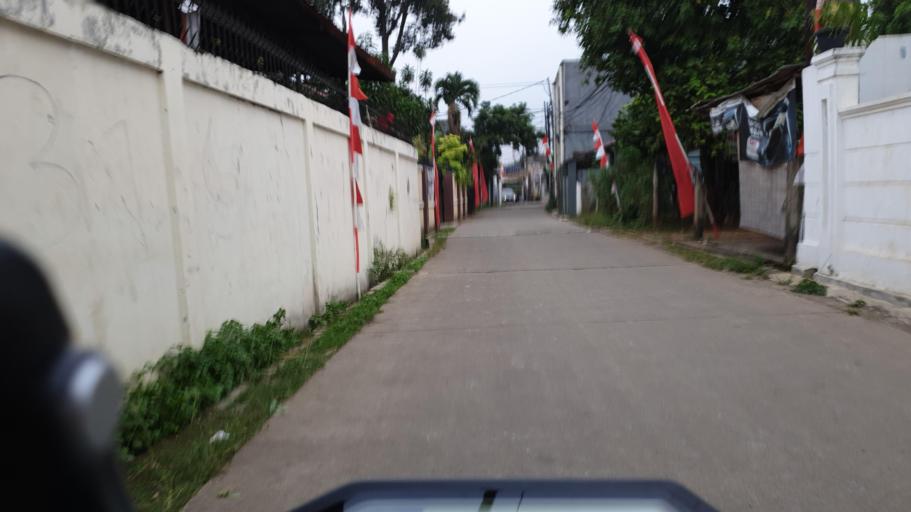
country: ID
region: West Java
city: Pamulang
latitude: -6.3221
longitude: 106.7700
